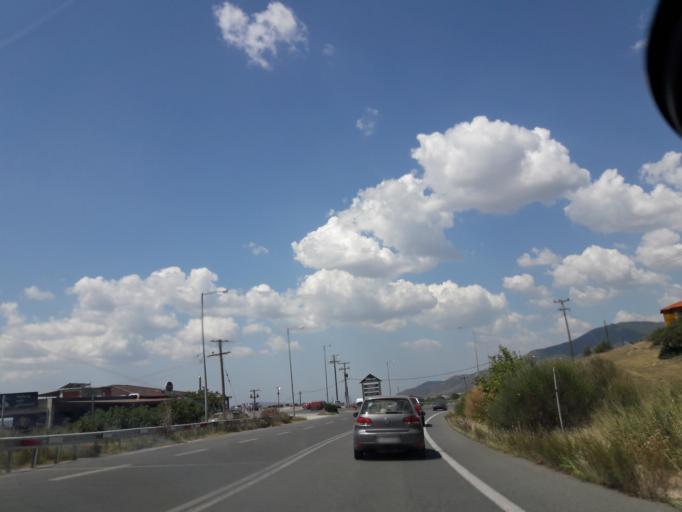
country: GR
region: Central Macedonia
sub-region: Nomos Chalkidikis
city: Galatista
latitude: 40.4573
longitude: 23.2920
